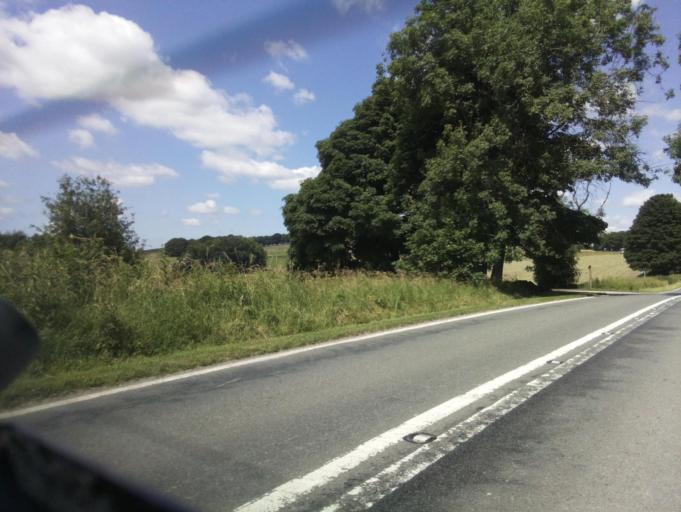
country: GB
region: England
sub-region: Derbyshire
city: Bakewell
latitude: 53.1319
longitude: -1.7548
